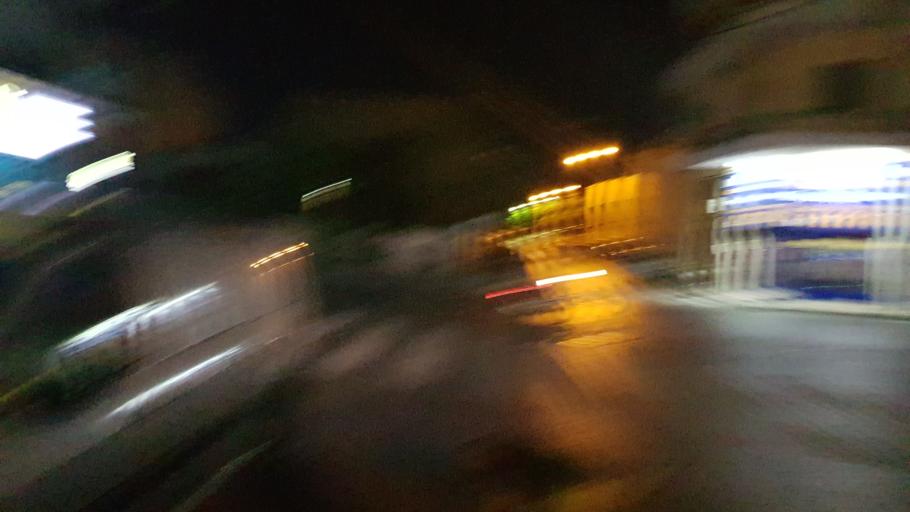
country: GR
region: Crete
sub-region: Nomos Irakleiou
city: Irakleion
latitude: 35.3385
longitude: 25.1464
